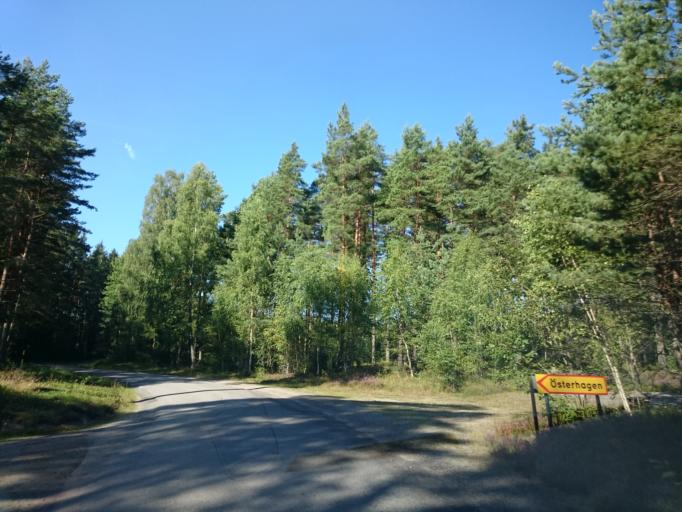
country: SE
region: Soedermanland
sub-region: Nykopings Kommun
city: Stigtomta
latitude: 58.6376
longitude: 16.6922
